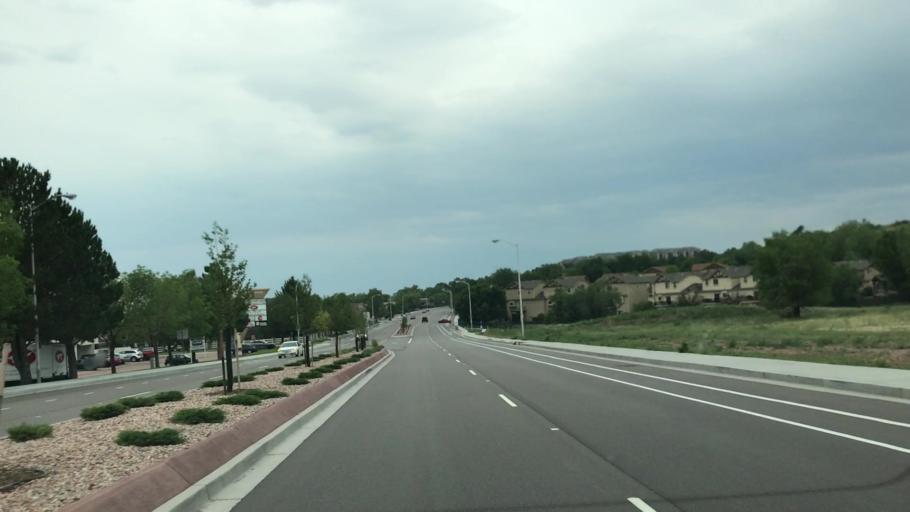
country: US
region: Colorado
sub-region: El Paso County
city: Colorado Springs
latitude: 38.8923
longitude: -104.8506
